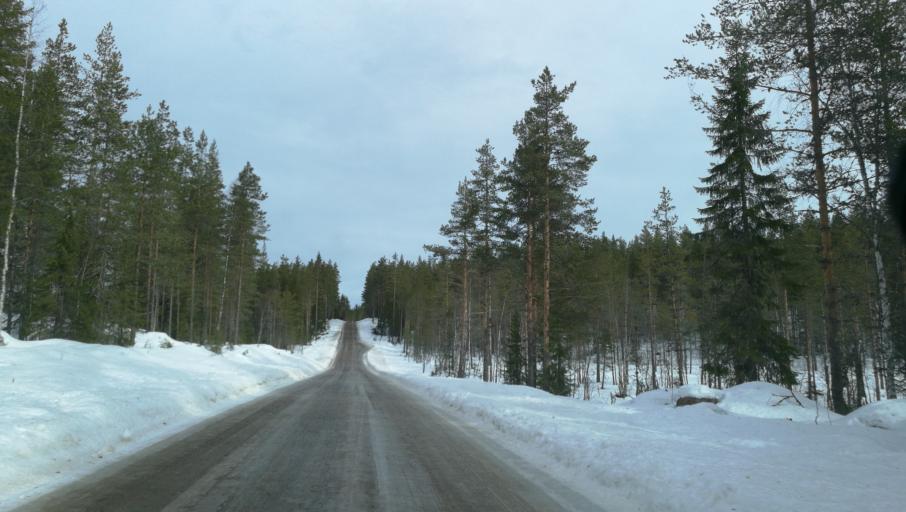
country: SE
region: Vaermland
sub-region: Torsby Kommun
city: Torsby
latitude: 60.6457
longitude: 12.7984
